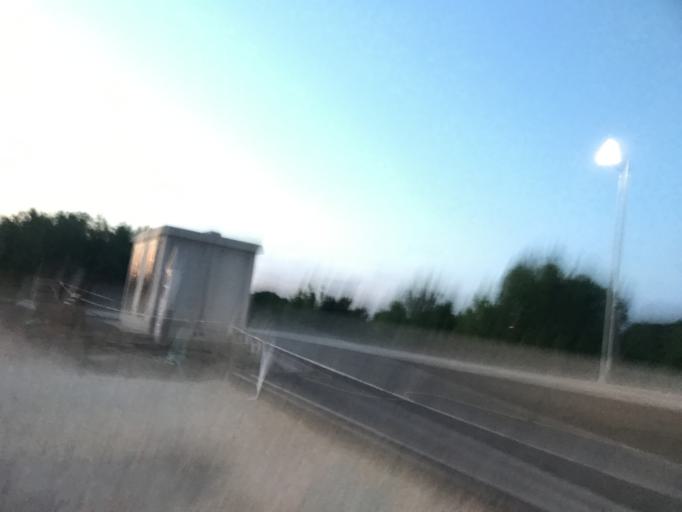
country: RS
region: Autonomna Pokrajina Vojvodina
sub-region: Juznobacki Okrug
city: Novi Sad
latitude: 45.2691
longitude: 19.8029
